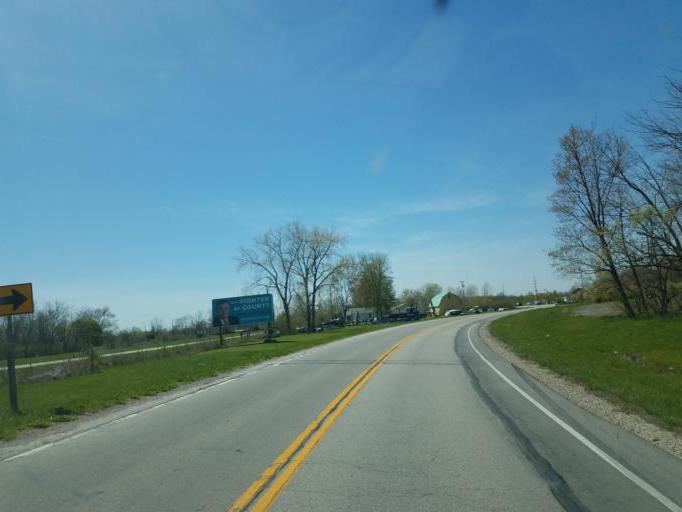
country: US
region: Ohio
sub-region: Ottawa County
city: Port Clinton
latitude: 41.5084
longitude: -82.8751
